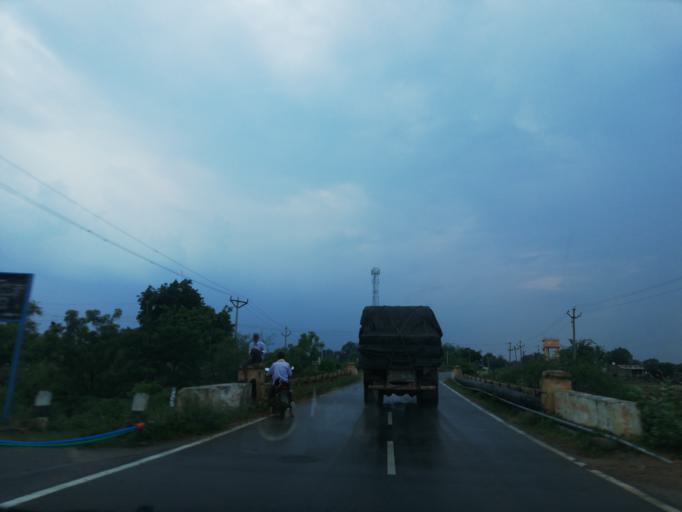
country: IN
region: Andhra Pradesh
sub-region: Guntur
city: Macherla
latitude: 16.6757
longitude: 79.2670
